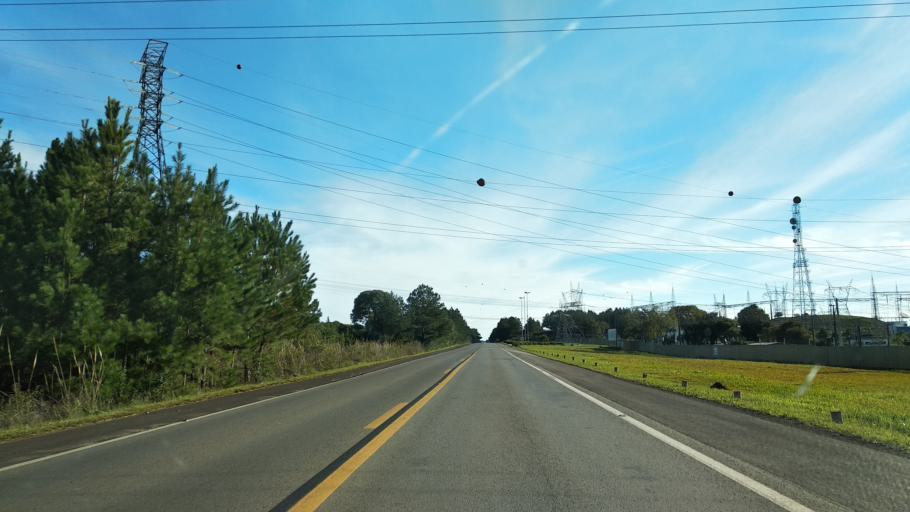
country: BR
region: Santa Catarina
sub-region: Celso Ramos
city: Celso Ramos
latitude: -27.5405
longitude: -51.4137
